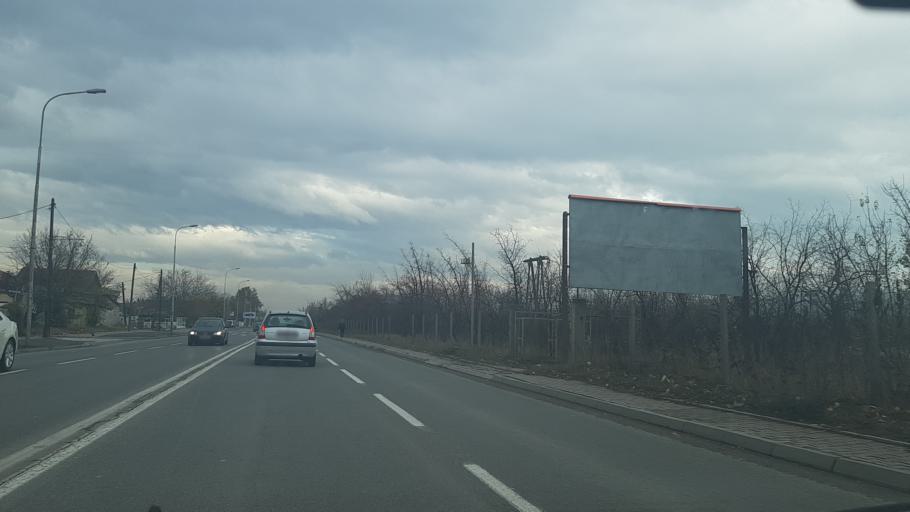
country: MK
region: Kisela Voda
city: Usje
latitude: 41.9771
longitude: 21.4494
